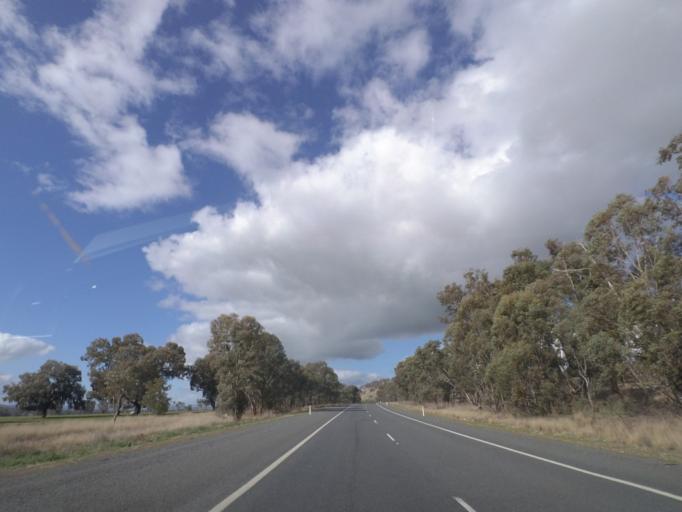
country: AU
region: New South Wales
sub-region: Greater Hume Shire
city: Holbrook
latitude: -35.6732
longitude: 147.3864
